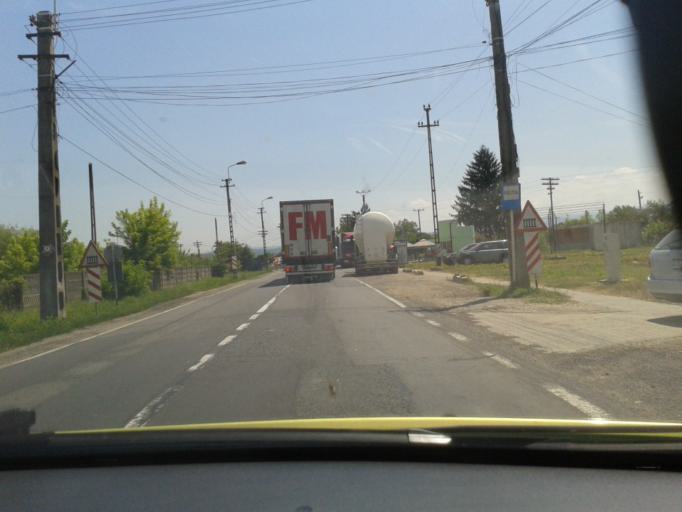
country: RO
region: Timis
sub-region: Comuna Margina
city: Margina
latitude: 45.8577
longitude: 22.2667
